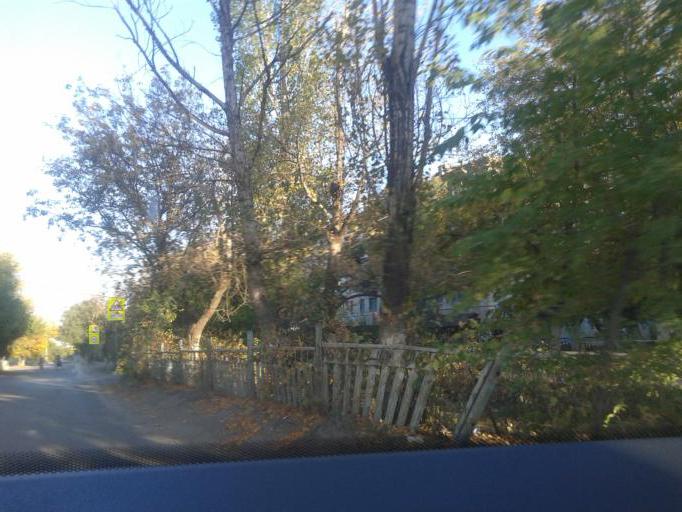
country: RU
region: Volgograd
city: Gorodishche
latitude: 48.7702
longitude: 44.4784
